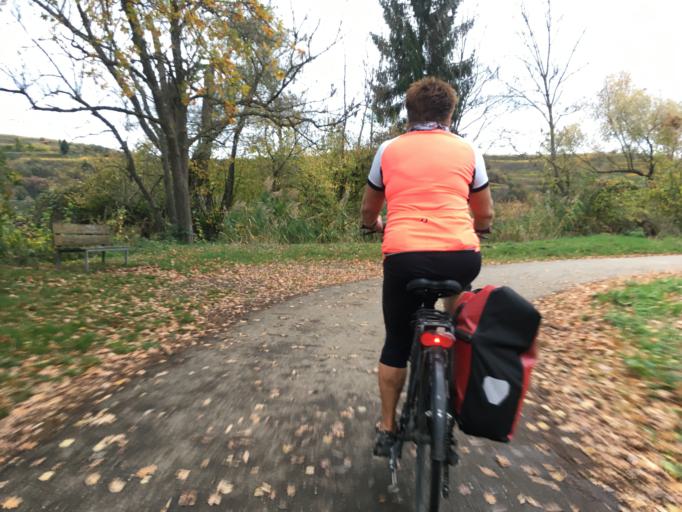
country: DE
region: Baden-Wuerttemberg
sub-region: Freiburg Region
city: Eichstetten
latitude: 48.0834
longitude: 7.7418
